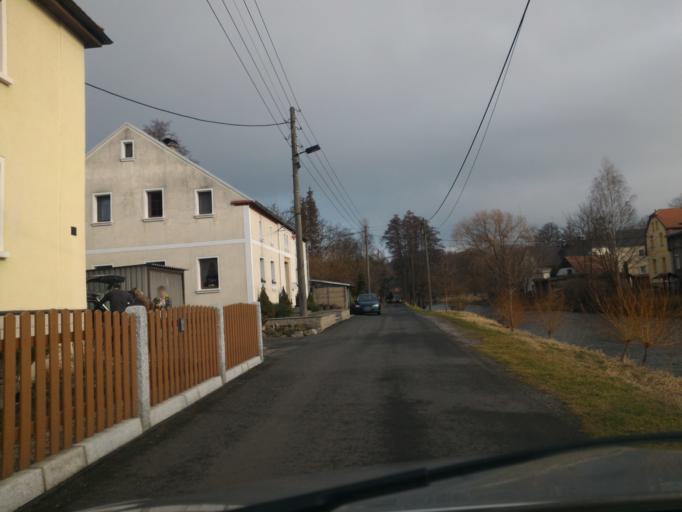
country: DE
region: Saxony
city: Grossschonau
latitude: 50.8966
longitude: 14.6883
